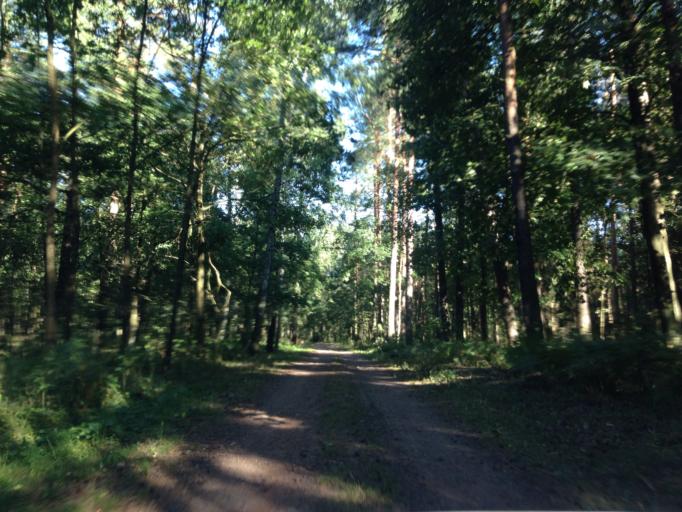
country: PL
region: Kujawsko-Pomorskie
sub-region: Powiat brodnicki
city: Gorzno
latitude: 53.1603
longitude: 19.6202
